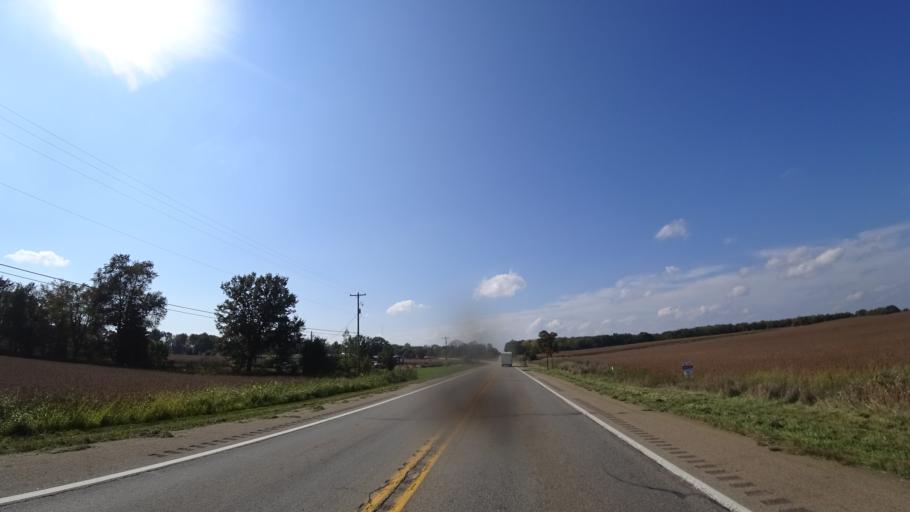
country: US
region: Michigan
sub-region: Calhoun County
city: Homer
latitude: 42.1618
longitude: -84.7387
